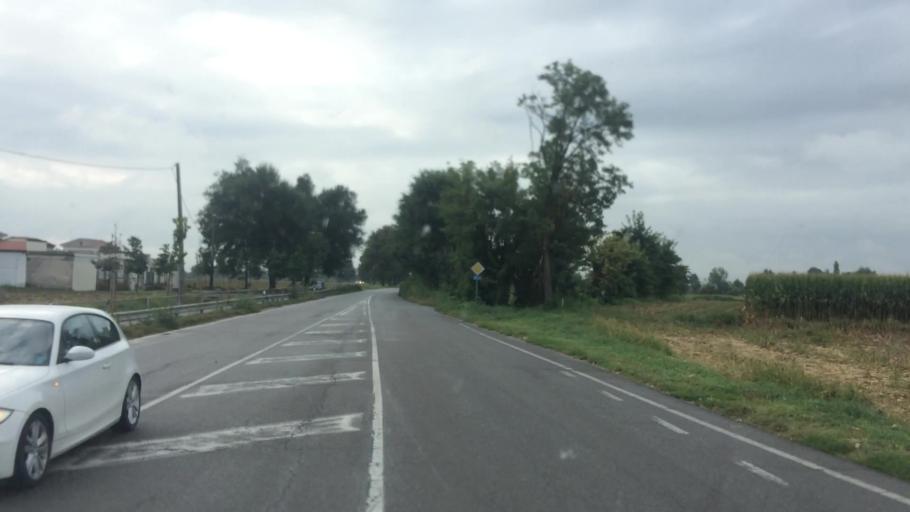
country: IT
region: Lombardy
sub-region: Provincia di Brescia
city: Longhena
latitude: 45.4335
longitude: 10.0614
